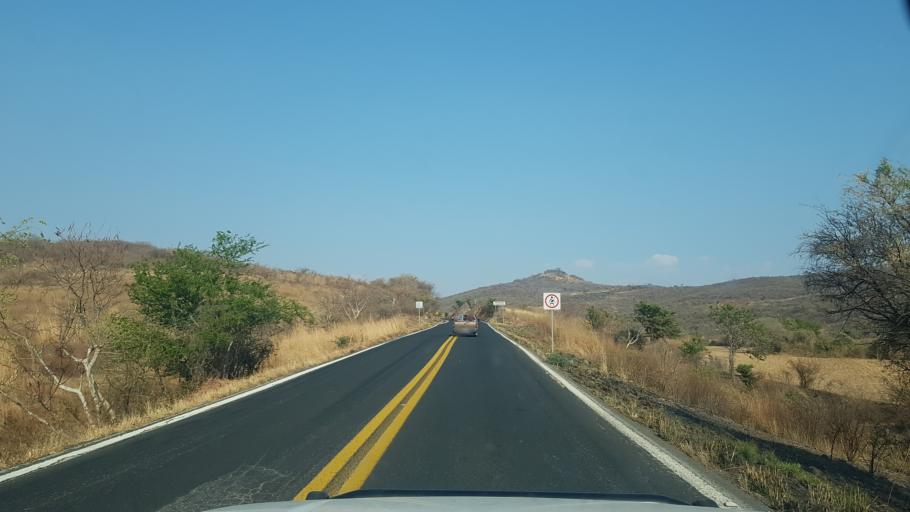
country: MX
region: Puebla
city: Calmeca
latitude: 18.6419
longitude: -98.6142
